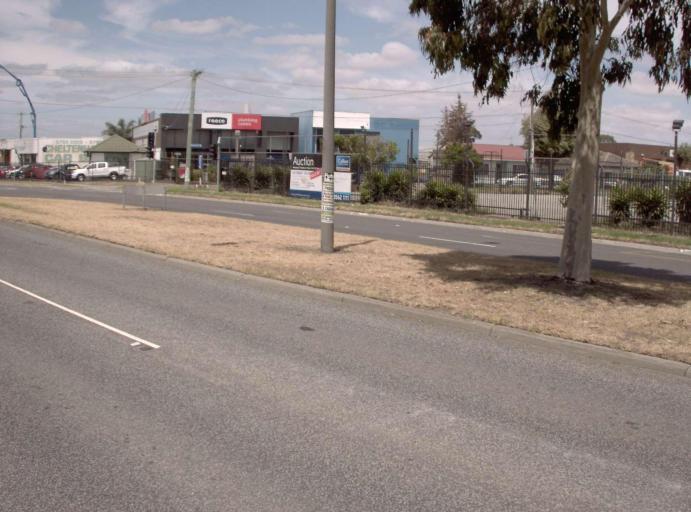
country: AU
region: Victoria
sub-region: Greater Dandenong
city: Dandenong
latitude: -37.9909
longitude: 145.1982
